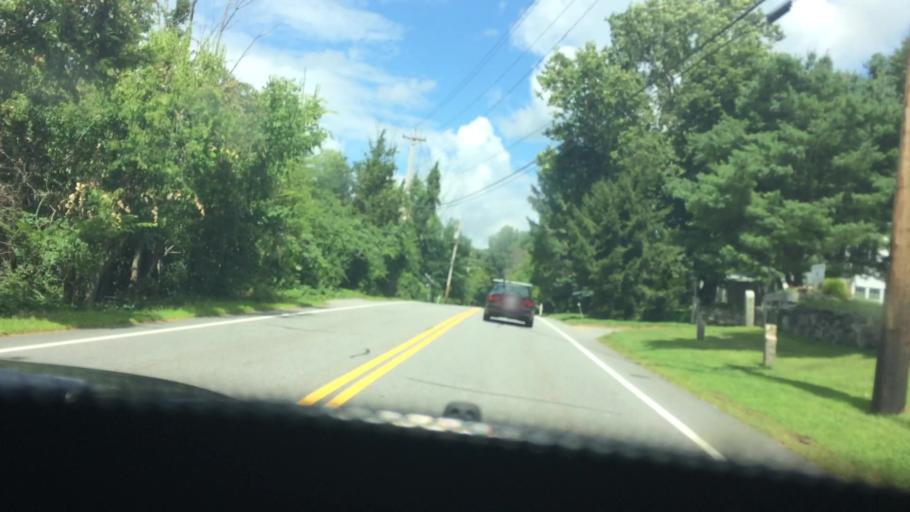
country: US
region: Massachusetts
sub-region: Middlesex County
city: Wayland
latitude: 42.3706
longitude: -71.3696
